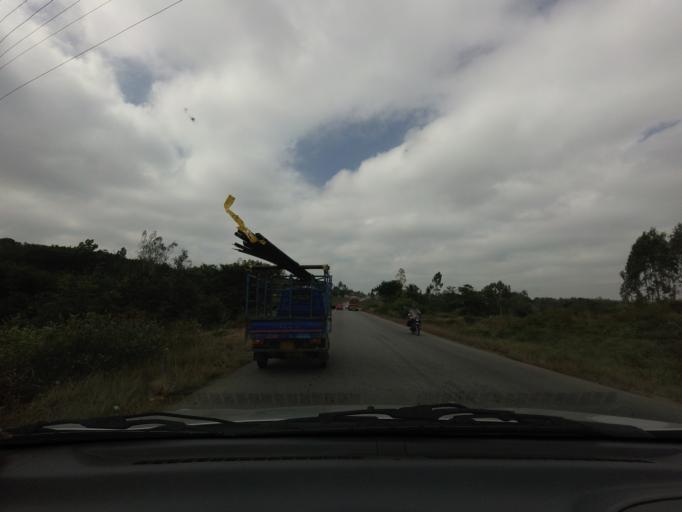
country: IN
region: Karnataka
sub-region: Hassan
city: Alur
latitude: 12.9492
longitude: 75.9631
